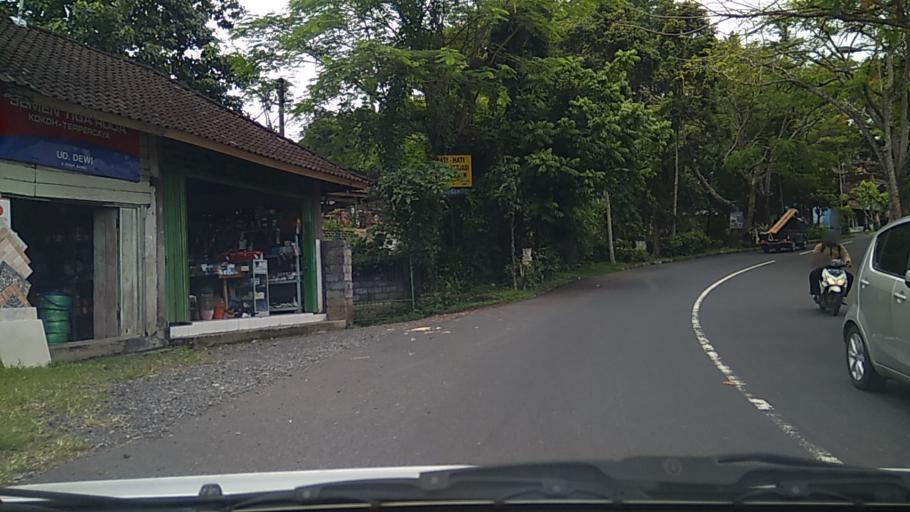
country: ID
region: Bali
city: Banjar Kelodan
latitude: -8.5257
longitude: 115.3469
